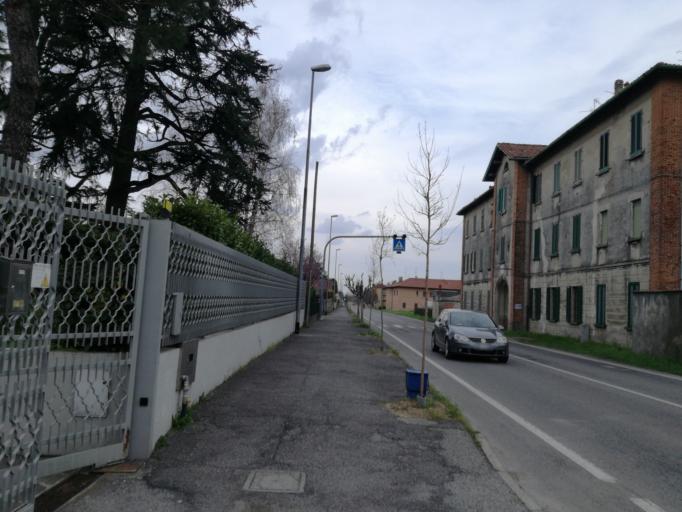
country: IT
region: Lombardy
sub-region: Provincia di Lecco
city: Verderio Superiore
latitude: 45.6651
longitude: 9.4453
